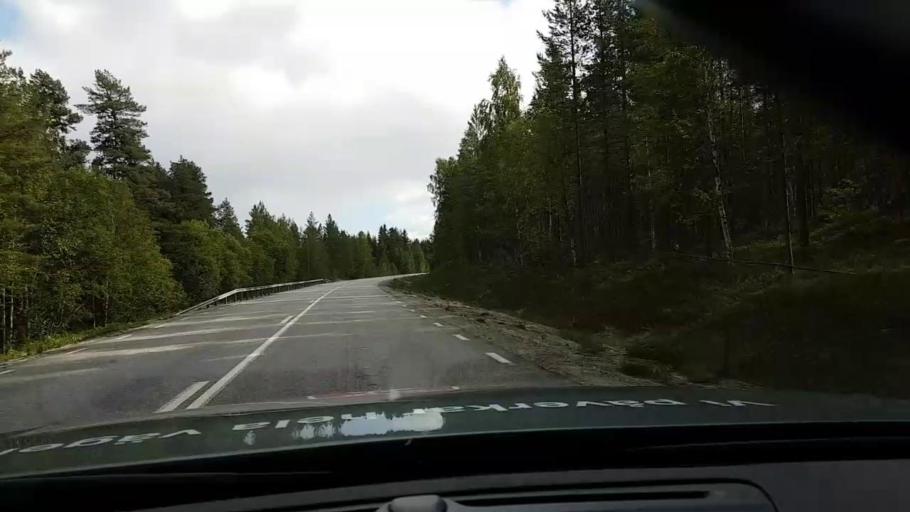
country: SE
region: Vaesternorrland
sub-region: OErnskoeldsviks Kommun
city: Bredbyn
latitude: 63.6346
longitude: 17.9069
